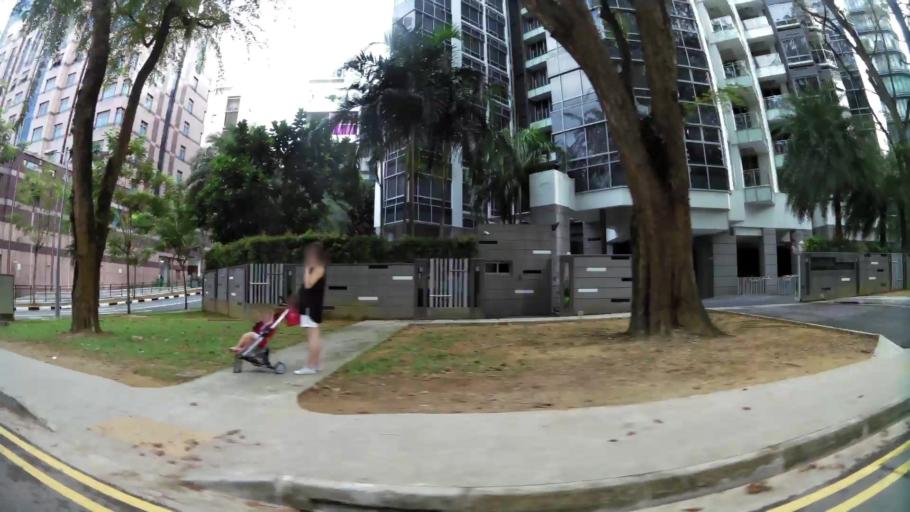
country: SG
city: Singapore
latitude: 1.2971
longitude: 103.8379
